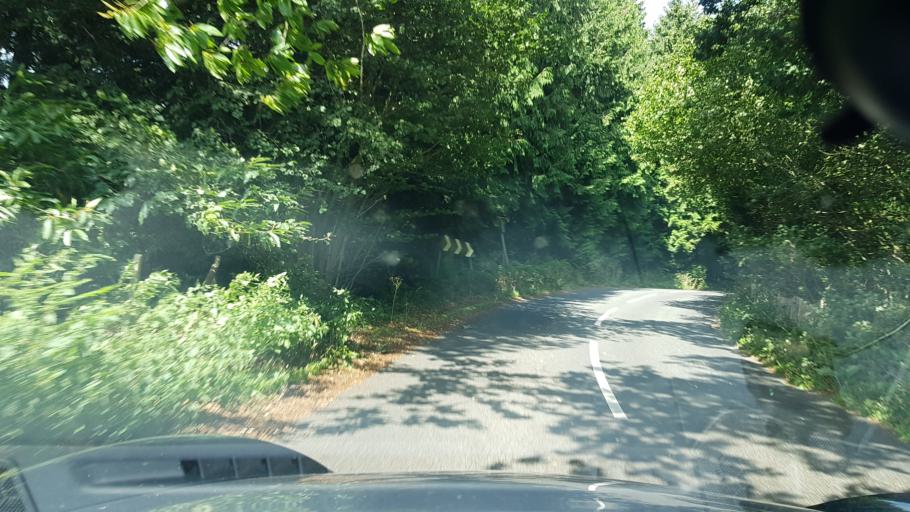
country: GB
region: England
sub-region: Surrey
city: Seale
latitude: 51.2131
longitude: -0.7205
